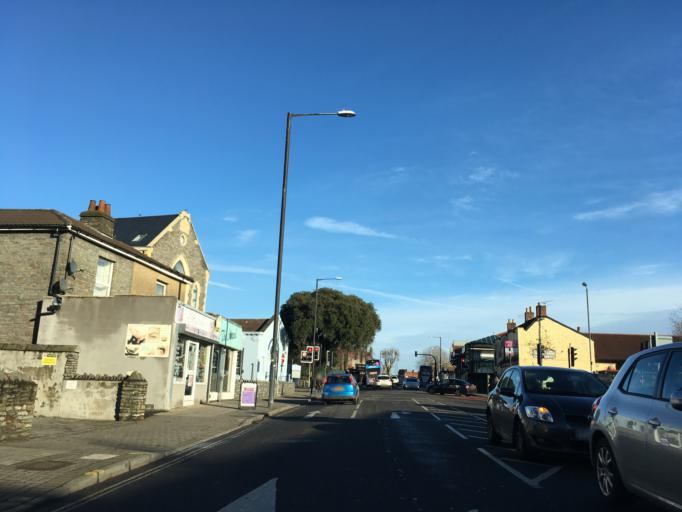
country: GB
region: England
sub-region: South Gloucestershire
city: Mangotsfield
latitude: 51.4785
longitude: -2.5340
